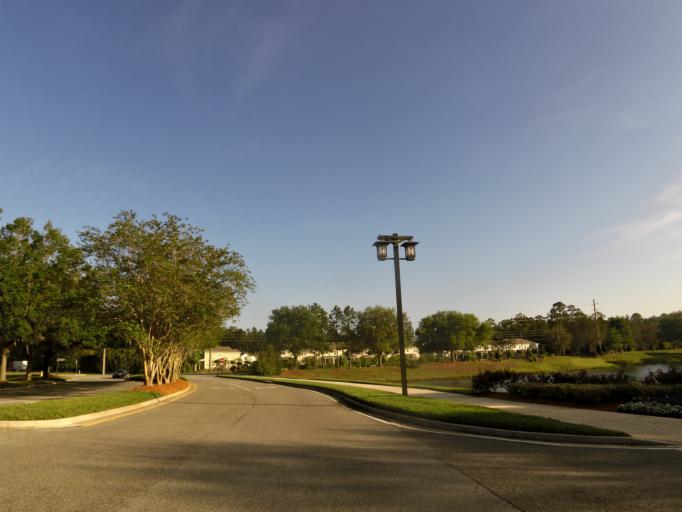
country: US
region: Florida
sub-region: Saint Johns County
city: Villano Beach
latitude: 29.9765
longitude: -81.4761
